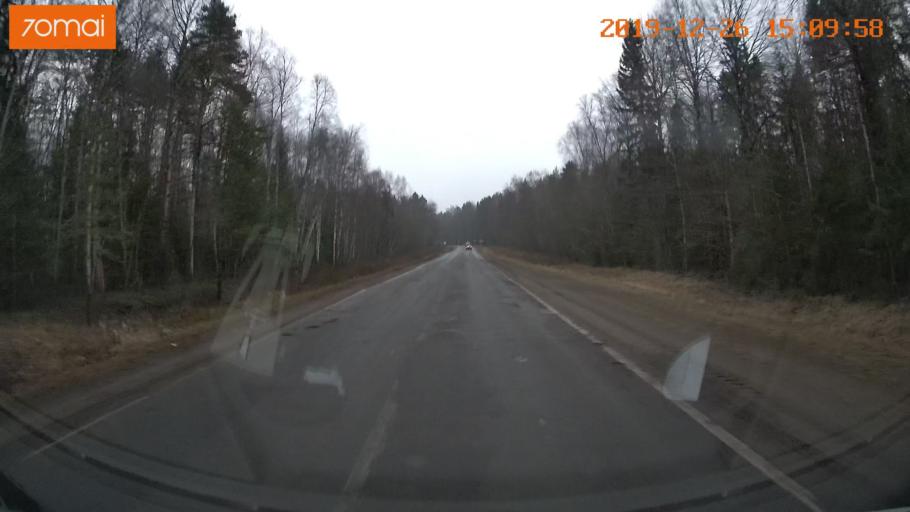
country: RU
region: Jaroslavl
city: Rybinsk
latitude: 58.1443
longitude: 38.8462
